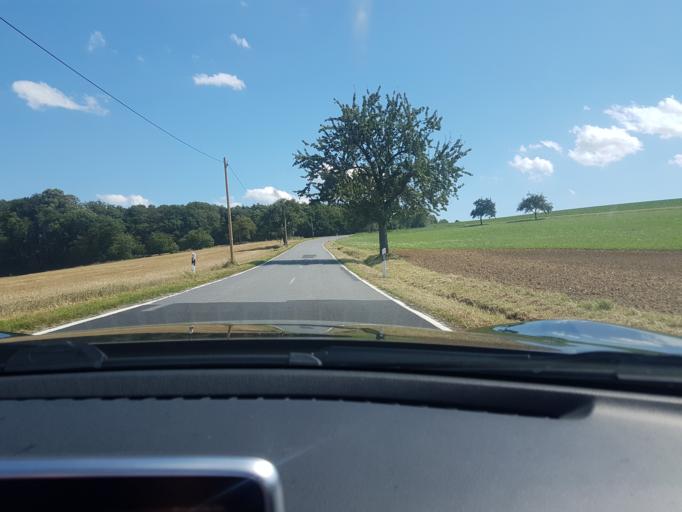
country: DE
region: Baden-Wuerttemberg
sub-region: Karlsruhe Region
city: Billigheim
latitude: 49.3365
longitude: 9.2670
